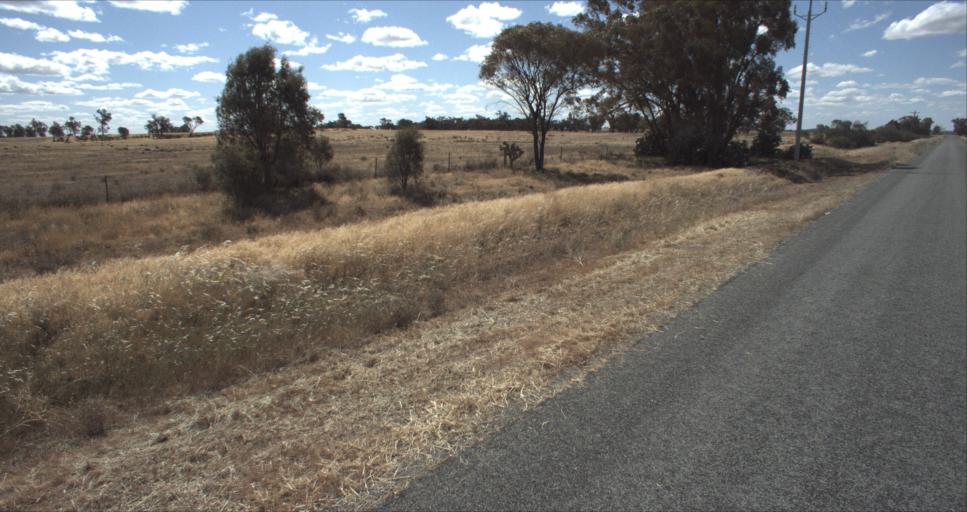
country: AU
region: New South Wales
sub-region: Leeton
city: Leeton
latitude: -34.4915
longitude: 146.2472
